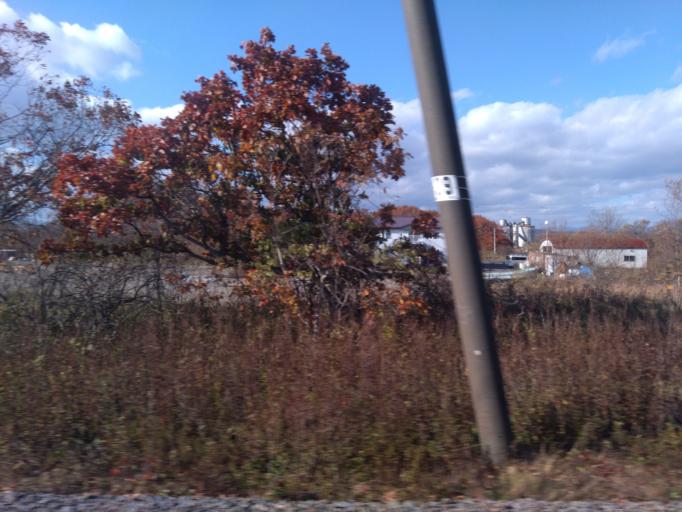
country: JP
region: Hokkaido
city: Shiraoi
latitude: 42.5363
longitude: 141.3300
